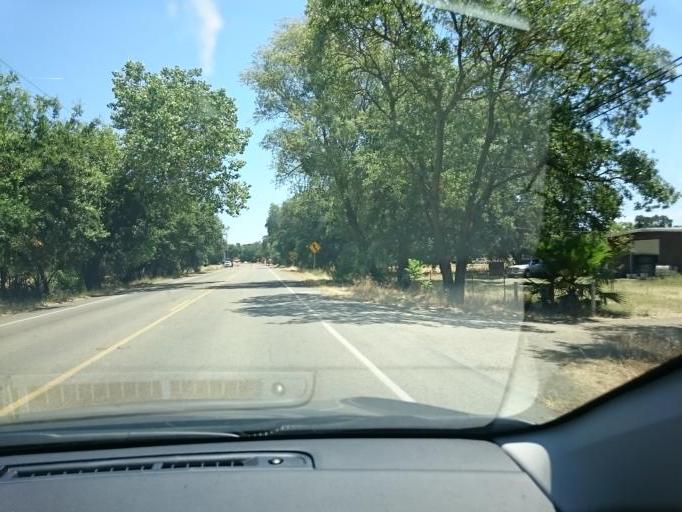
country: US
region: California
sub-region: San Joaquin County
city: Thornton
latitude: 38.2255
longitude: -121.4491
